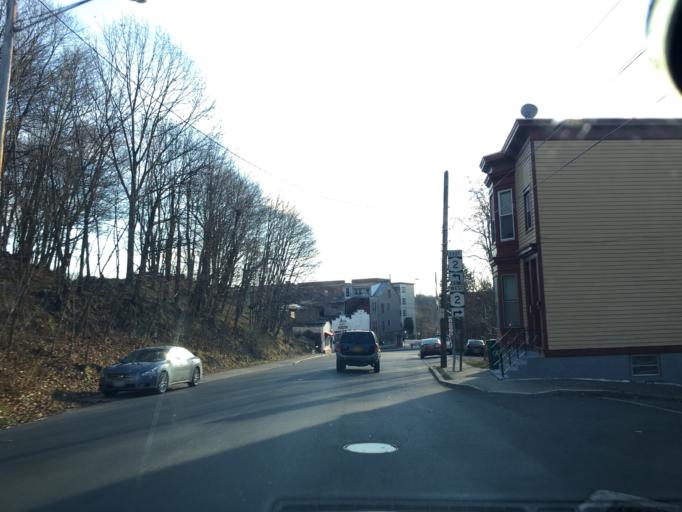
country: US
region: New York
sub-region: Rensselaer County
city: Troy
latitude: 42.7237
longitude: -73.6791
